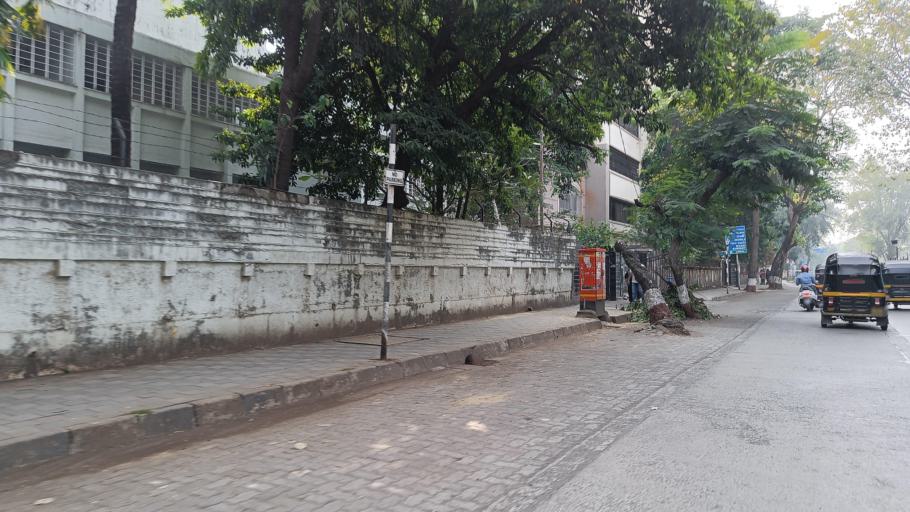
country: IN
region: Maharashtra
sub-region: Mumbai Suburban
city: Mumbai
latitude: 19.1058
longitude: 72.8370
